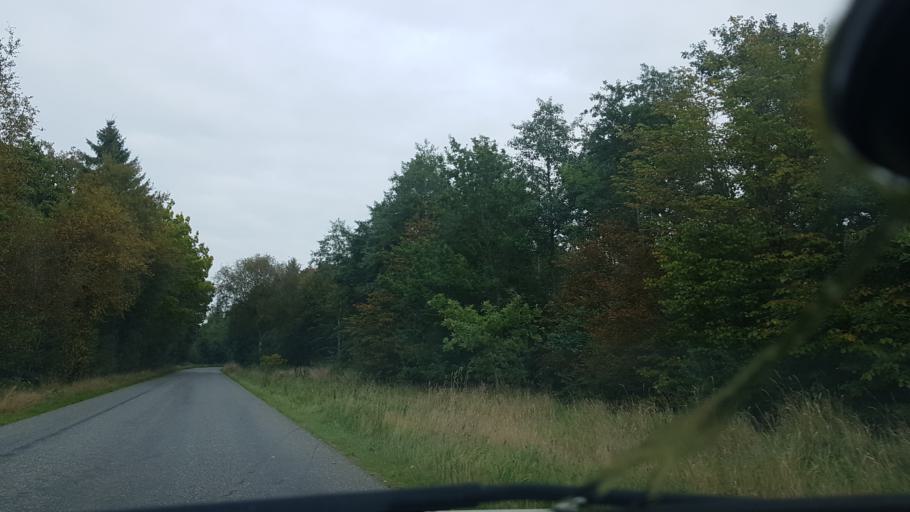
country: DK
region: South Denmark
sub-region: Vejen Kommune
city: Vejen
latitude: 55.5815
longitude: 9.1741
